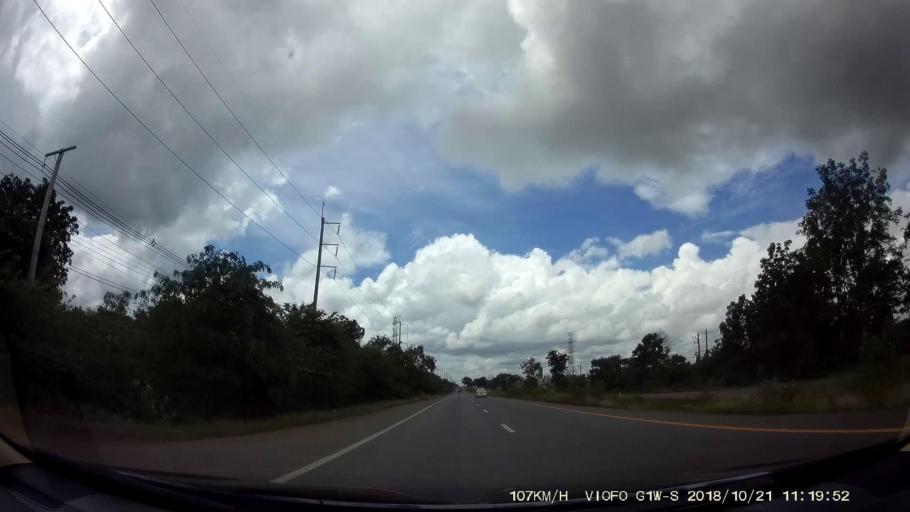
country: TH
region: Chaiyaphum
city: Chaiyaphum
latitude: 15.8631
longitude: 102.0813
